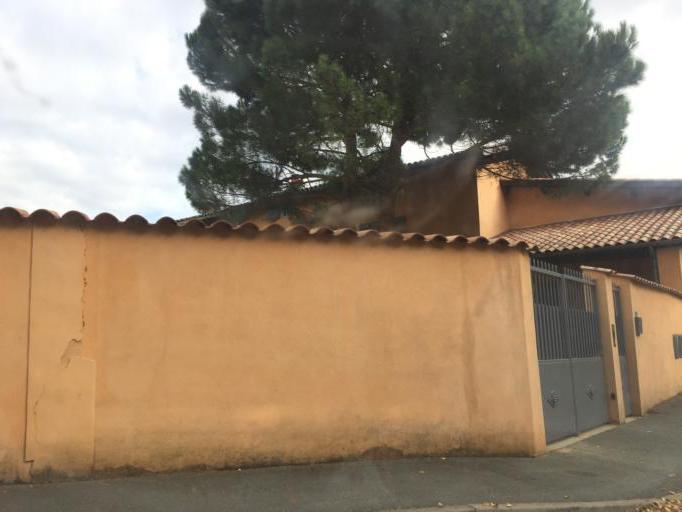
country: FR
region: Rhone-Alpes
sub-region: Departement du Rhone
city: Montanay
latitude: 45.8783
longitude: 4.8673
